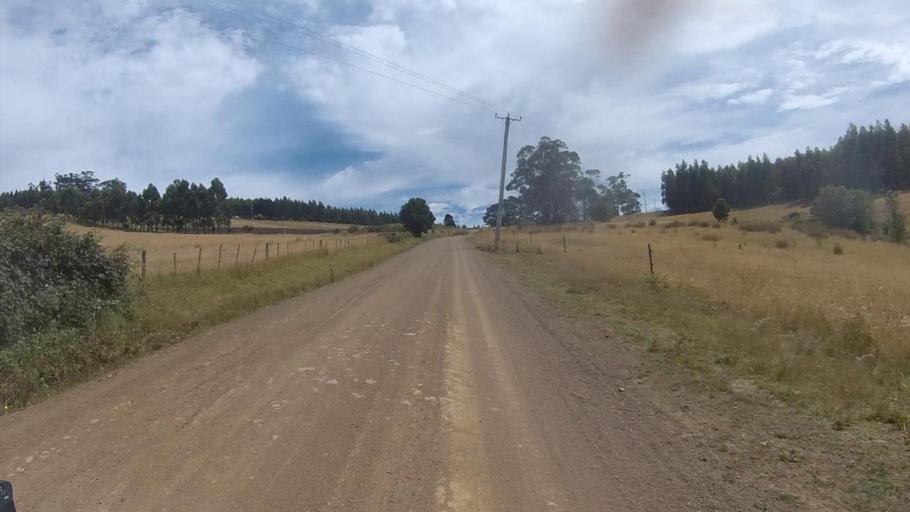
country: AU
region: Tasmania
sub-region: Sorell
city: Sorell
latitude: -42.7854
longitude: 147.8429
